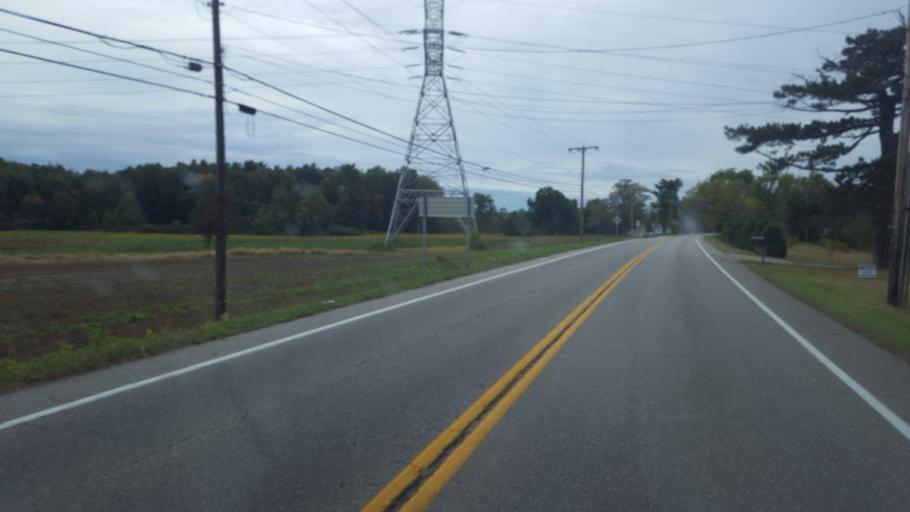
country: US
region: Ohio
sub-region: Lorain County
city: Lorain
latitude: 41.4090
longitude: -82.1691
